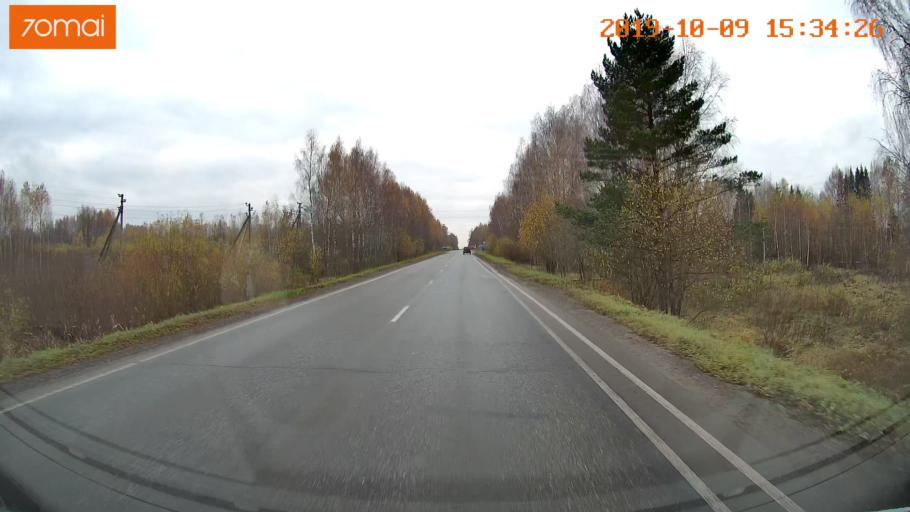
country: RU
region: Kostroma
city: Oktyabr'skiy
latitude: 57.9408
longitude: 41.2447
